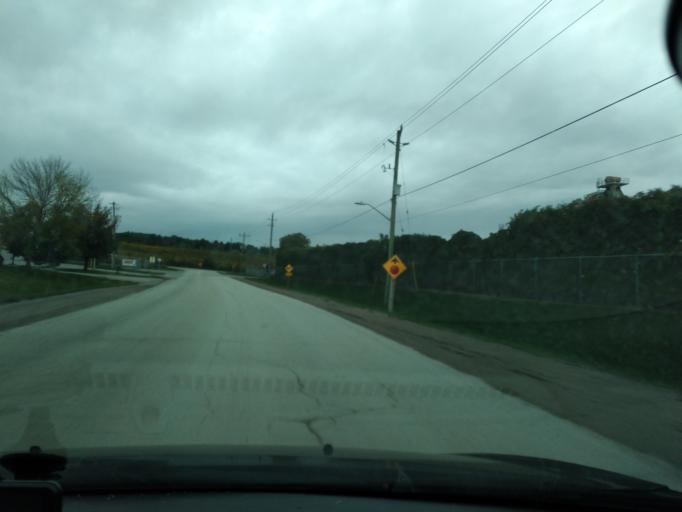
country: CA
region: Ontario
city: Bradford West Gwillimbury
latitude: 44.1404
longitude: -79.5561
